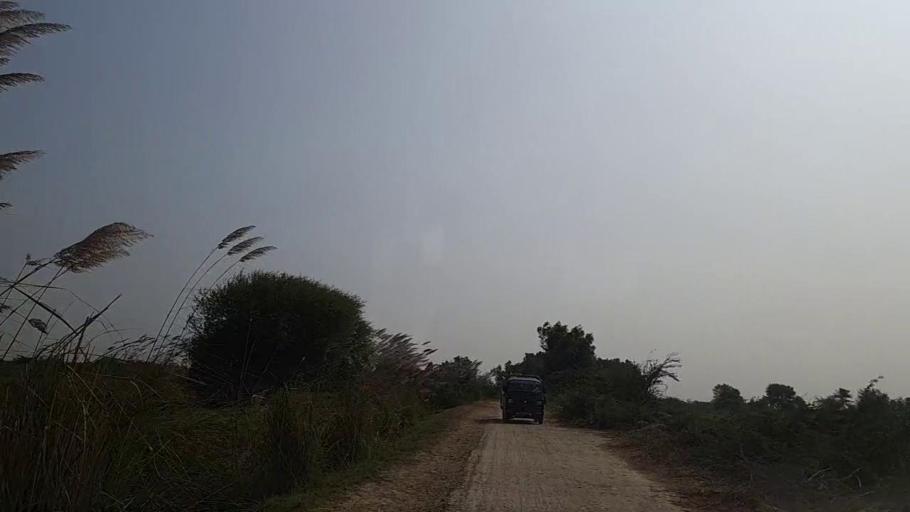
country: PK
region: Sindh
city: Mirpur Sakro
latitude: 24.5934
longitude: 67.7175
